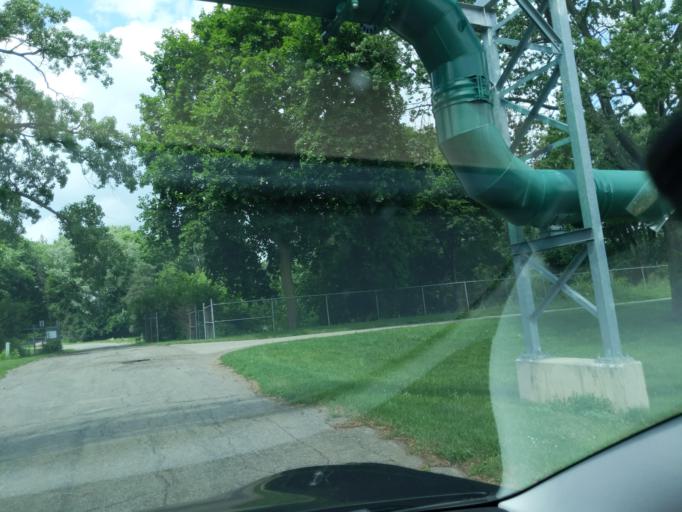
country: US
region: Michigan
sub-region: Jackson County
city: Jackson
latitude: 42.2828
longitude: -84.4104
